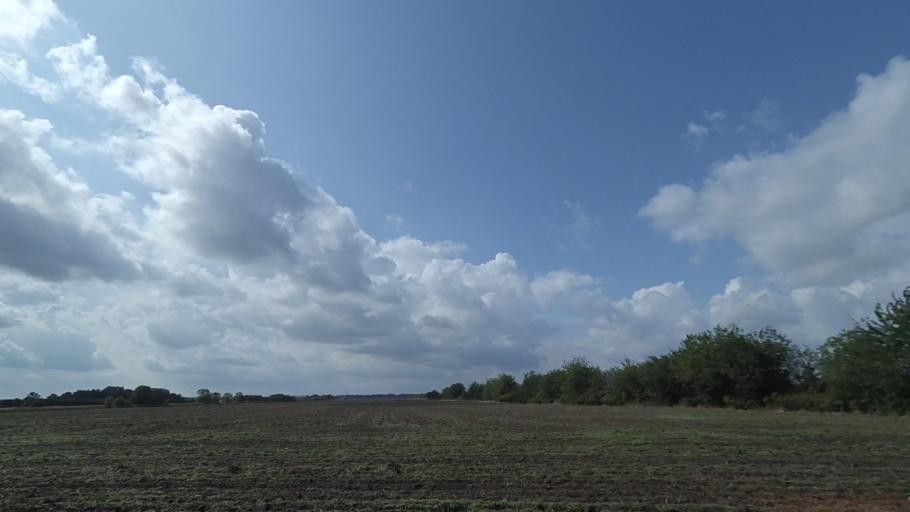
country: DK
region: Central Jutland
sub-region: Norddjurs Kommune
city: Allingabro
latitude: 56.5077
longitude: 10.3986
